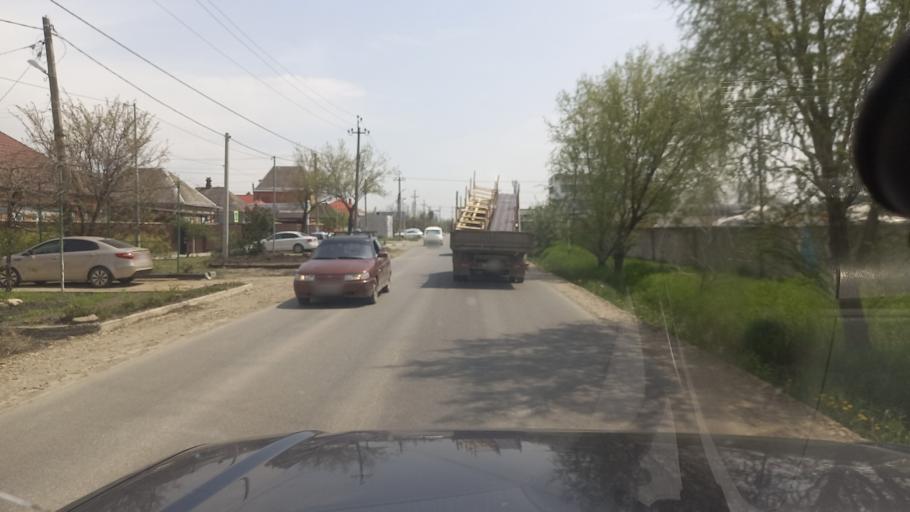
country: RU
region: Adygeya
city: Yablonovskiy
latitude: 44.9884
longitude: 38.9563
